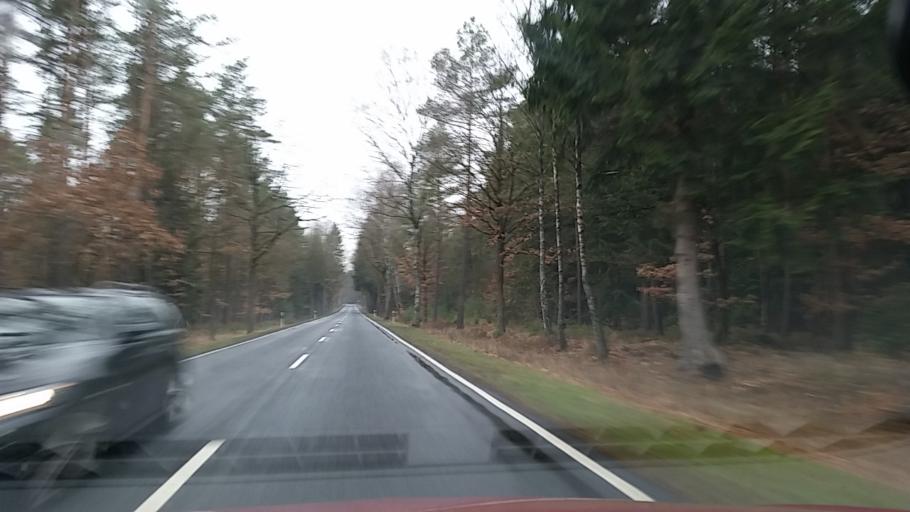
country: DE
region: Lower Saxony
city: Sprakensehl
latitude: 52.7829
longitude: 10.4160
